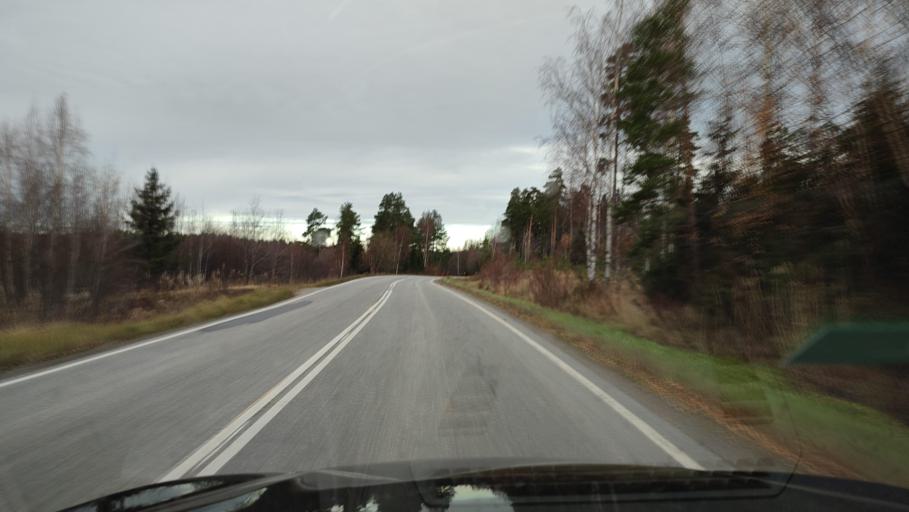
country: FI
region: Ostrobothnia
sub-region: Sydosterbotten
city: Naerpes
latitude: 62.4117
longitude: 21.3484
